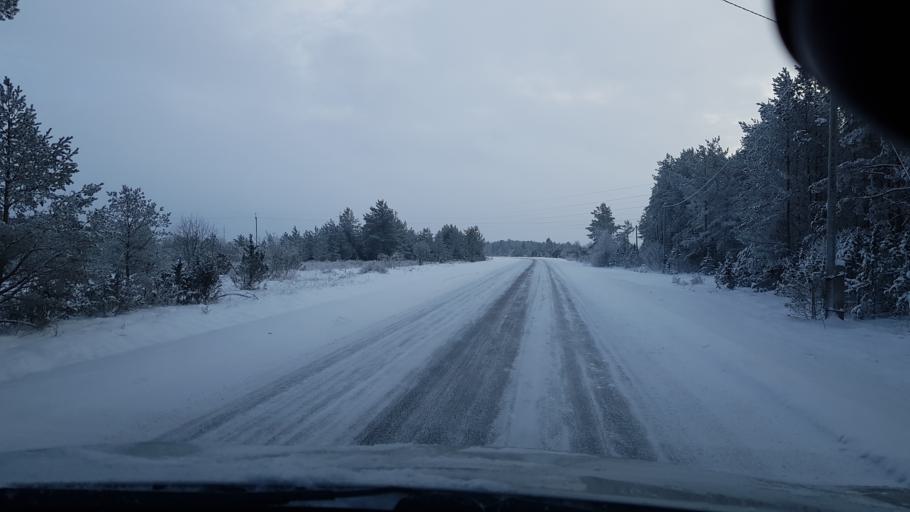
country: EE
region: Harju
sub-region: Keila linn
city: Keila
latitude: 59.3521
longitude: 24.4272
